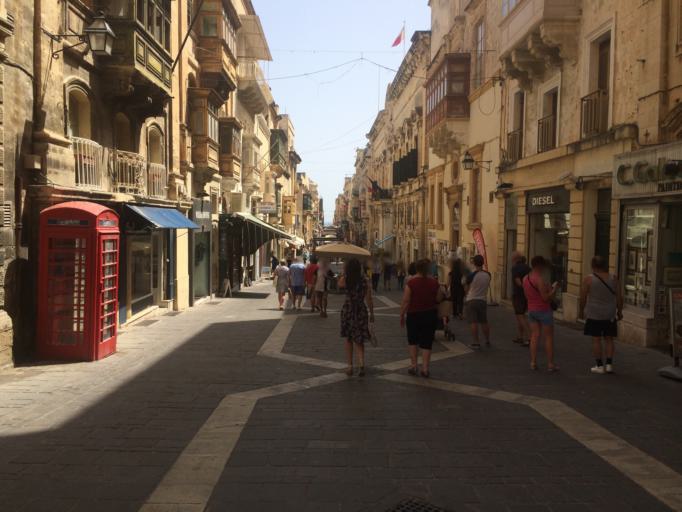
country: MT
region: Il-Furjana
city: Floriana
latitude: 35.8966
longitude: 14.5118
